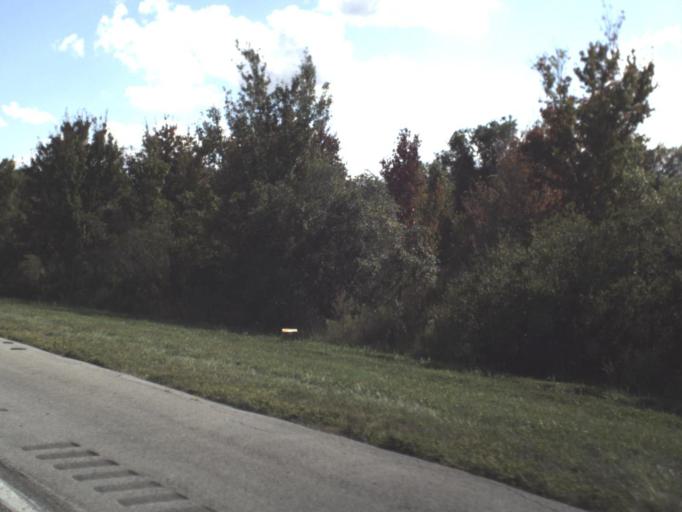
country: US
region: Florida
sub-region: Indian River County
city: Fellsmere
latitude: 27.7438
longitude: -80.9309
